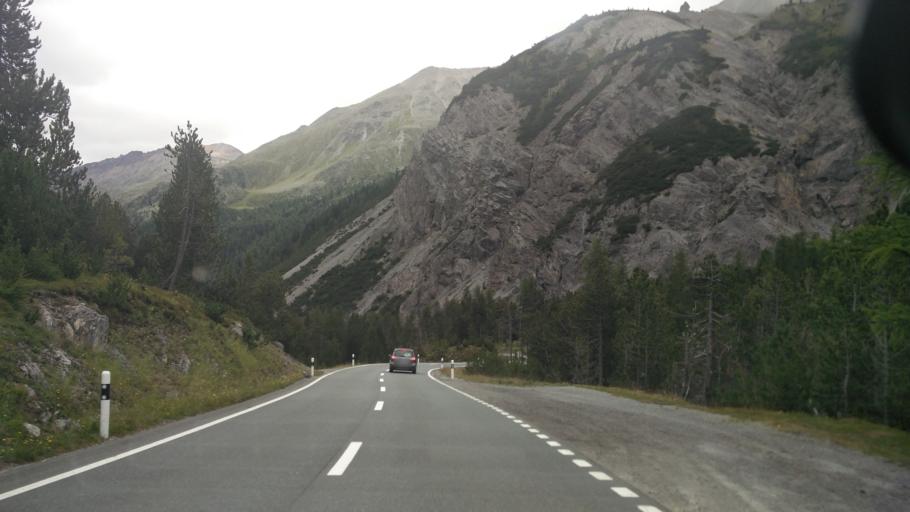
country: IT
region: Lombardy
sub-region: Provincia di Sondrio
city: Isolaccia
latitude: 46.6366
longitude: 10.3016
